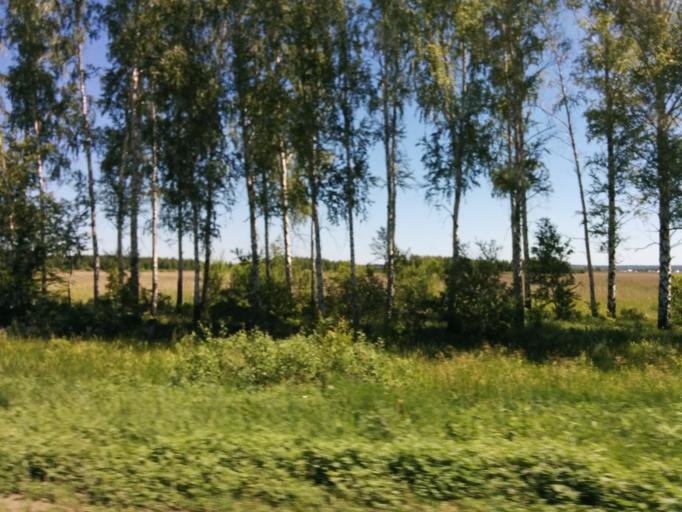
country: RU
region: Tambov
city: Goreloye
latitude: 52.9382
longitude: 41.4628
